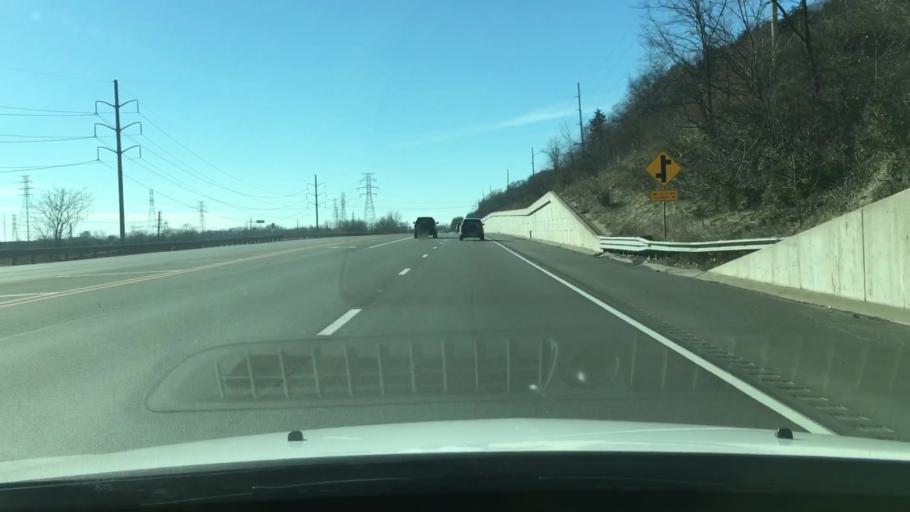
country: US
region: Illinois
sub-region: Tazewell County
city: Pekin
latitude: 40.6042
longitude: -89.6650
